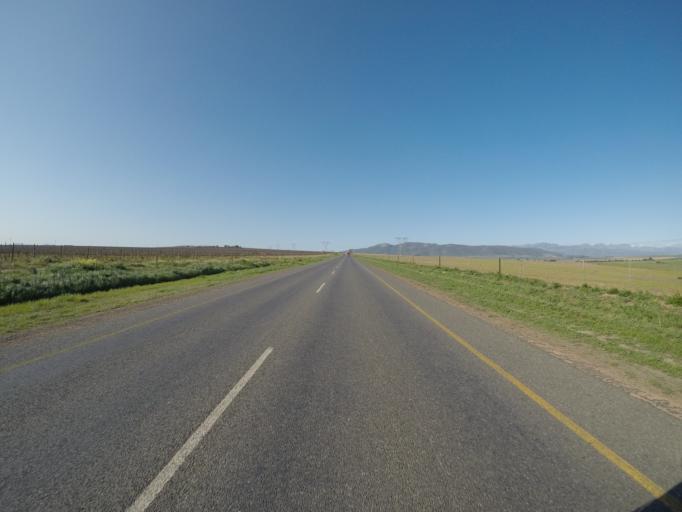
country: ZA
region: Western Cape
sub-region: City of Cape Town
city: Kraaifontein
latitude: -33.7562
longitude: 18.8155
